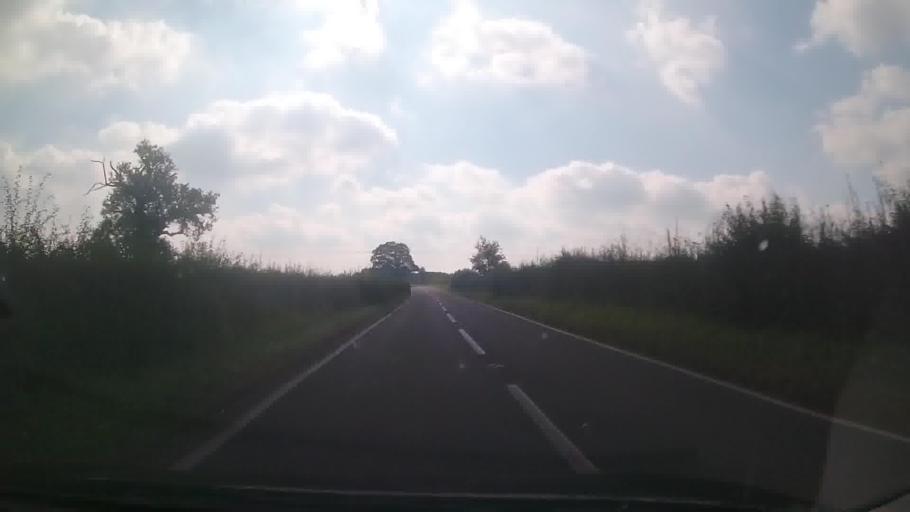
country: GB
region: England
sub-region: Cheshire West and Chester
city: Beeston
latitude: 53.0754
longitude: -2.6610
